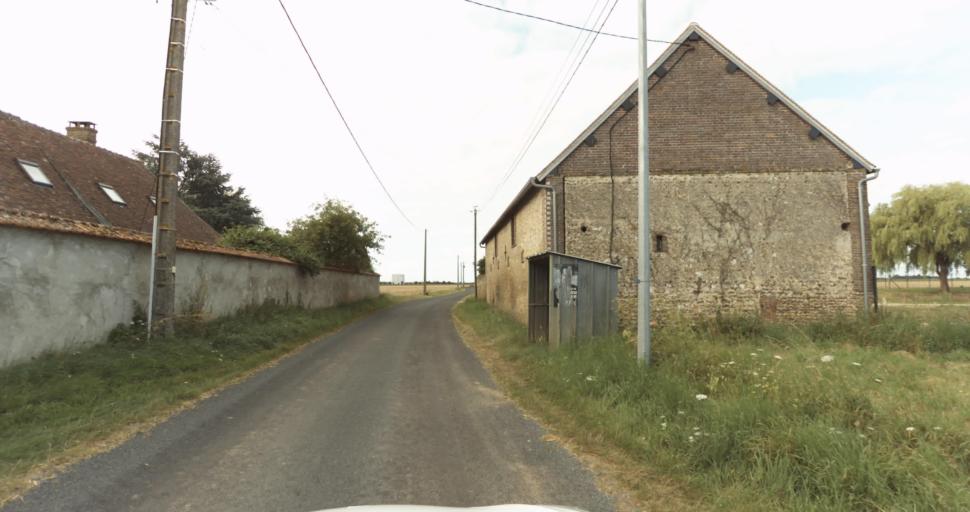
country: FR
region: Haute-Normandie
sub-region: Departement de l'Eure
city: La Madeleine-de-Nonancourt
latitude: 48.8440
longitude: 1.1909
